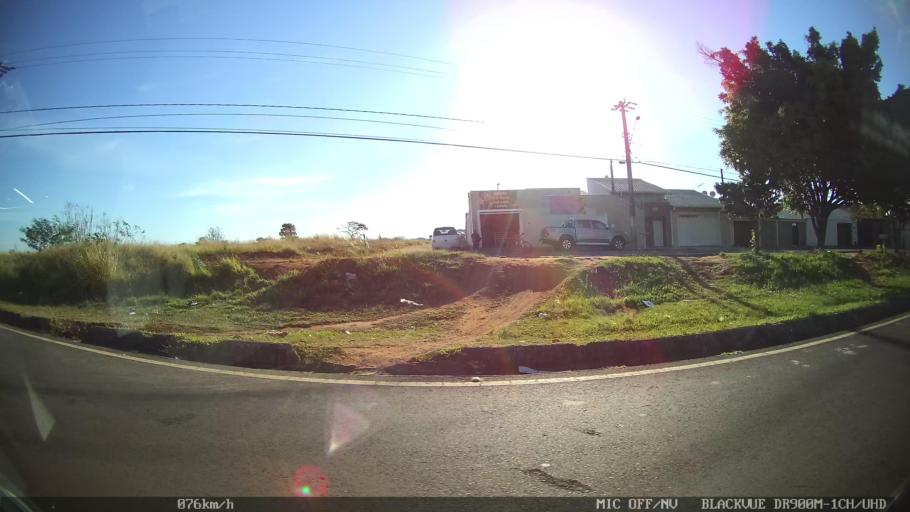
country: BR
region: Sao Paulo
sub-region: Franca
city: Franca
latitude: -20.5054
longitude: -47.3714
